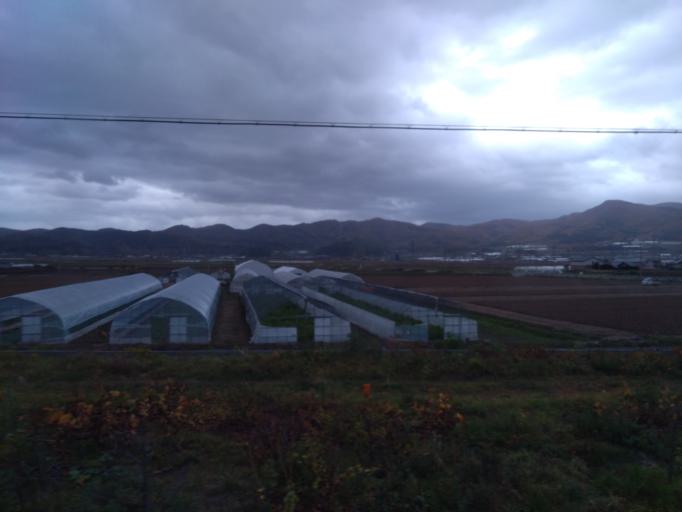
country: JP
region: Hokkaido
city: Nanae
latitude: 41.9037
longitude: 140.6534
